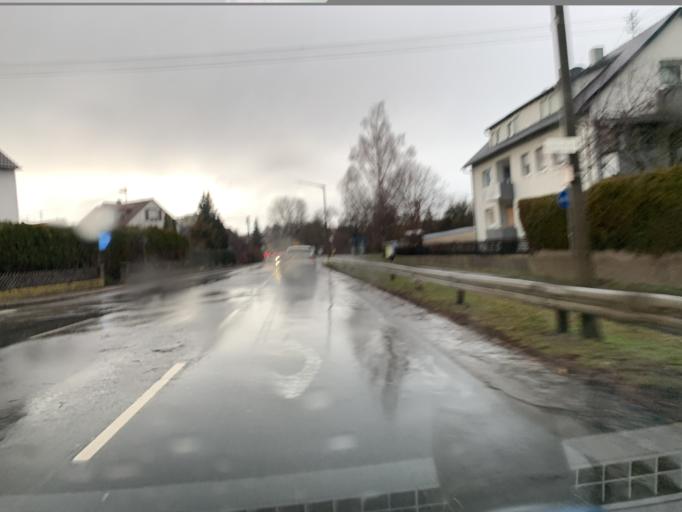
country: DE
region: Baden-Wuerttemberg
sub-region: Regierungsbezirk Stuttgart
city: Magstadt
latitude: 48.7163
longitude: 8.9719
